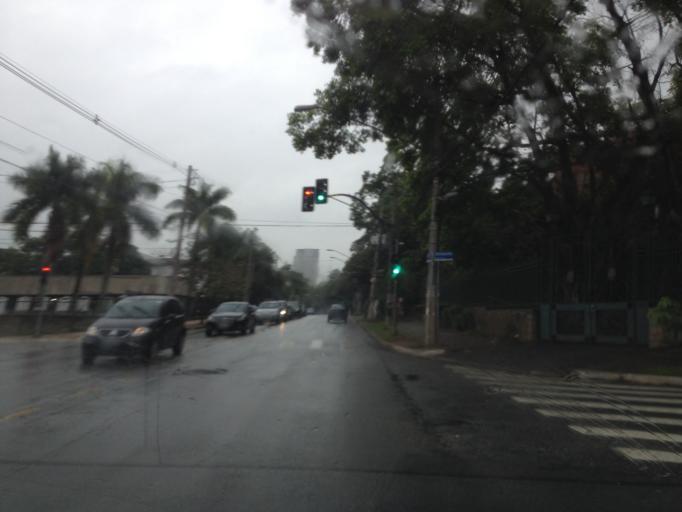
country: BR
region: Sao Paulo
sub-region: Sao Paulo
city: Sao Paulo
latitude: -23.5742
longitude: -46.6770
